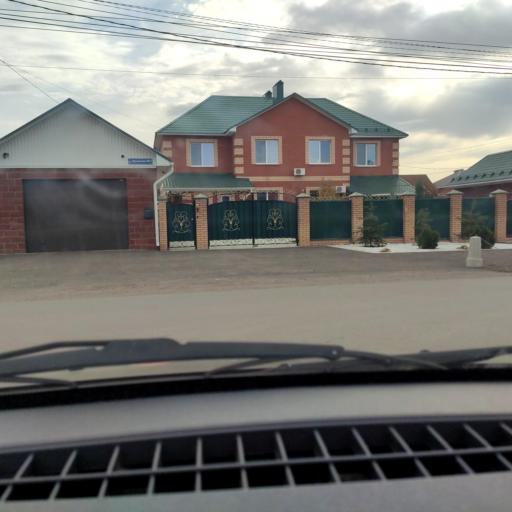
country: RU
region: Bashkortostan
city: Ufa
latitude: 54.6291
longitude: 55.9093
